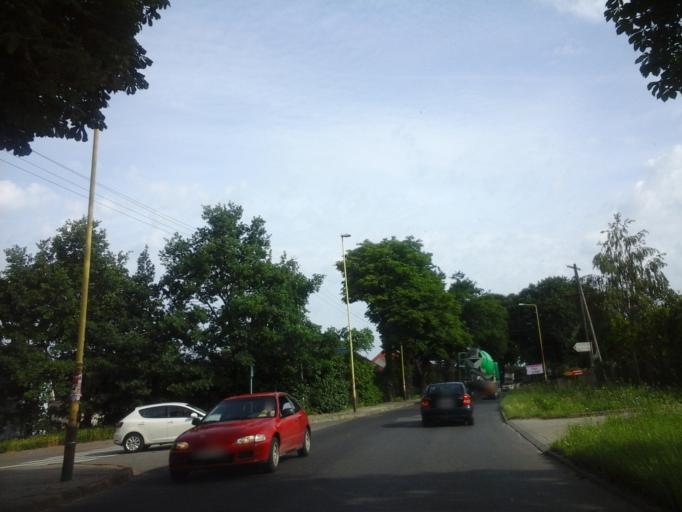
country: PL
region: West Pomeranian Voivodeship
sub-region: Powiat stargardzki
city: Stargard Szczecinski
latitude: 53.3156
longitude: 15.0408
